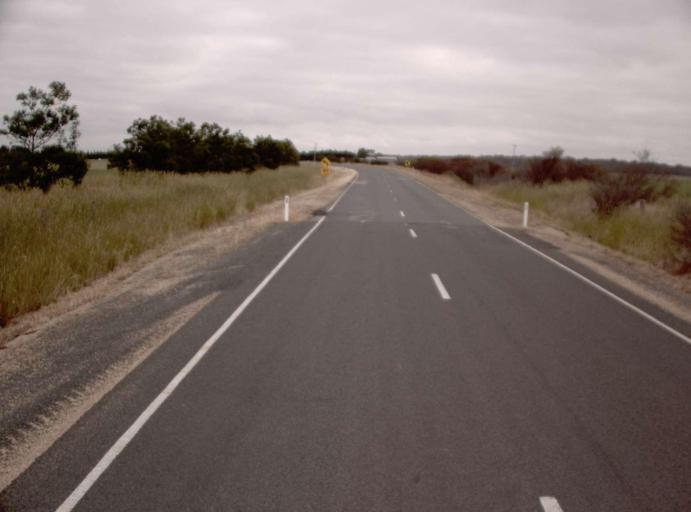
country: AU
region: Victoria
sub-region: Wellington
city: Sale
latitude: -38.0816
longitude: 146.9886
